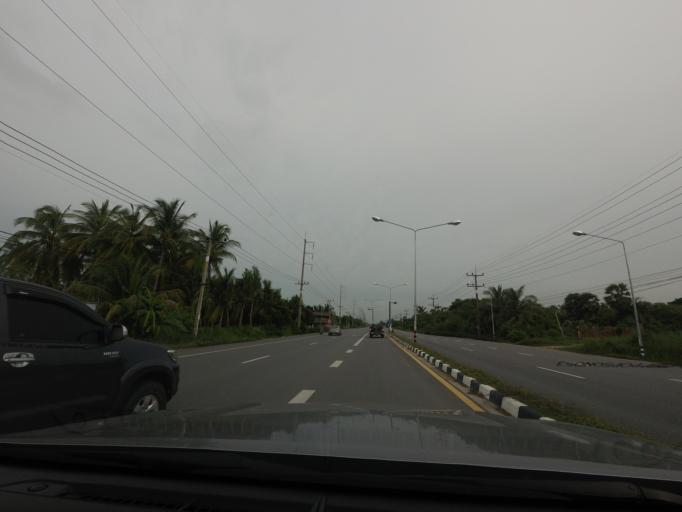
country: TH
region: Songkhla
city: Ranot
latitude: 7.7381
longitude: 100.3646
